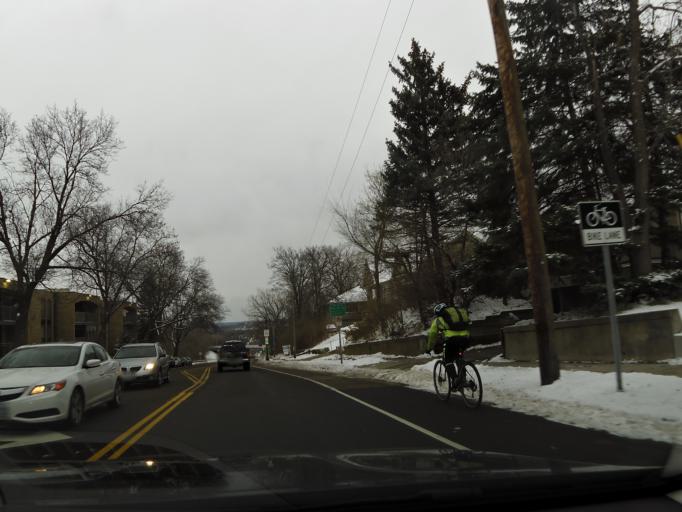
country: US
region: Minnesota
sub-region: Dakota County
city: West Saint Paul
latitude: 44.9305
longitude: -93.1465
